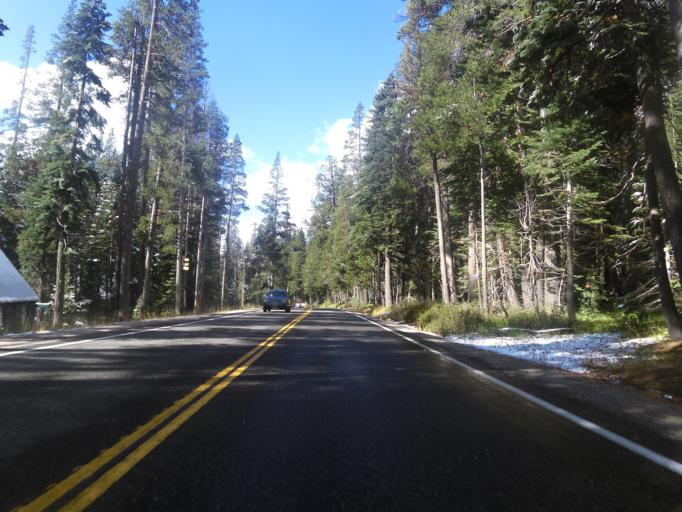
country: US
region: California
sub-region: El Dorado County
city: South Lake Tahoe
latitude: 38.8173
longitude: -120.0799
